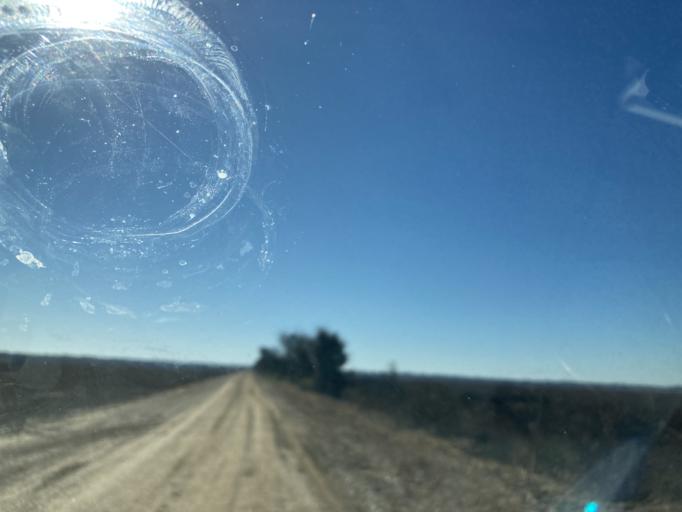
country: US
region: Mississippi
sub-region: Sharkey County
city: Rolling Fork
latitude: 32.8499
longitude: -90.6723
